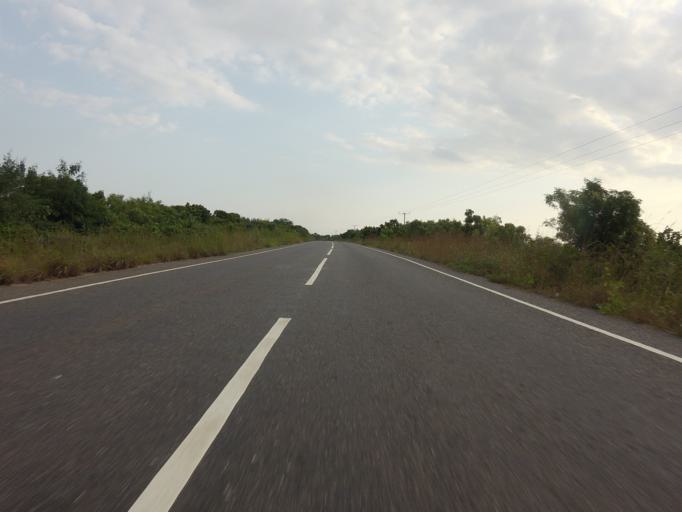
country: GH
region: Volta
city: Ho
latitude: 6.1089
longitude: 0.5158
